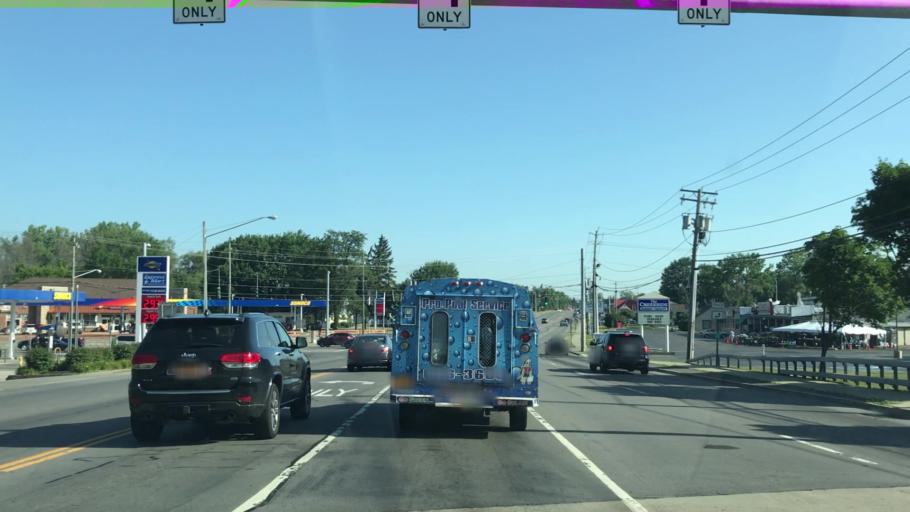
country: US
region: New York
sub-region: Erie County
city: Cheektowaga
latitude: 42.8843
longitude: -78.7545
